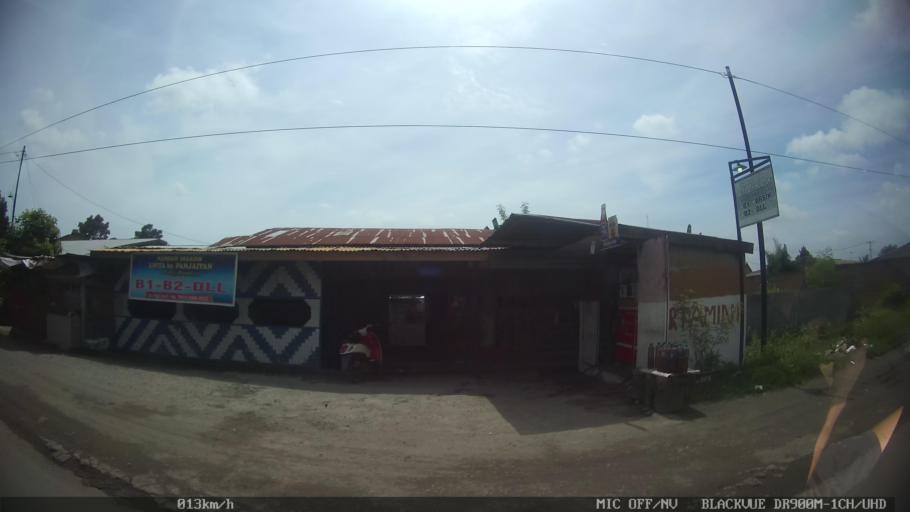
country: ID
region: North Sumatra
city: Medan
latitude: 3.6501
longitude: 98.7089
